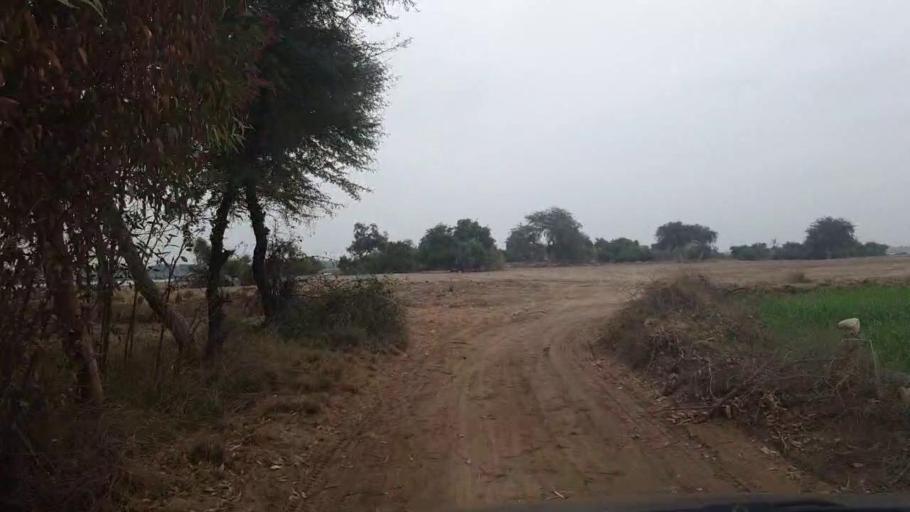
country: PK
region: Sindh
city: Shahdadpur
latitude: 25.8598
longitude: 68.6998
